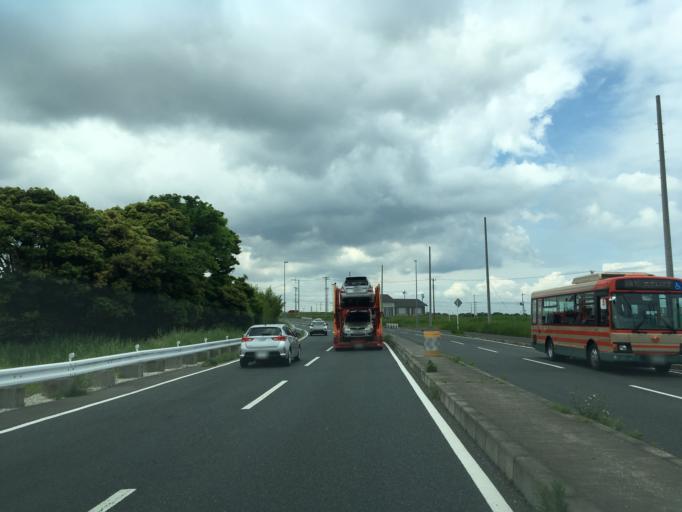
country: JP
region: Chiba
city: Kisarazu
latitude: 35.4250
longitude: 139.9212
